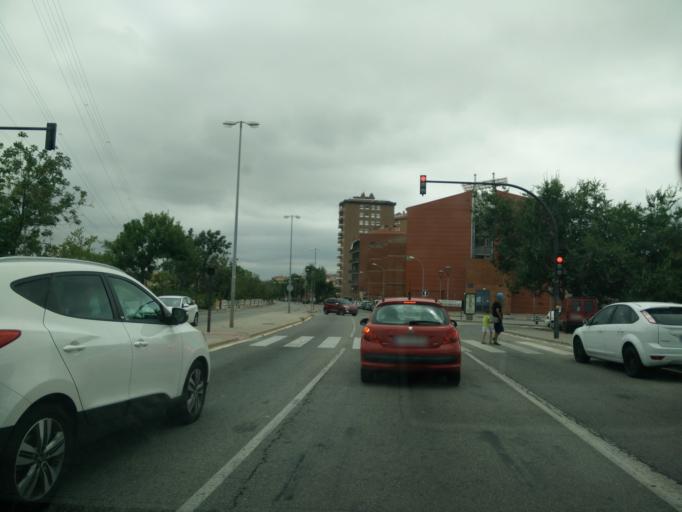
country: ES
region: Catalonia
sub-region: Provincia de Barcelona
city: Terrassa
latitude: 41.5779
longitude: 2.0278
